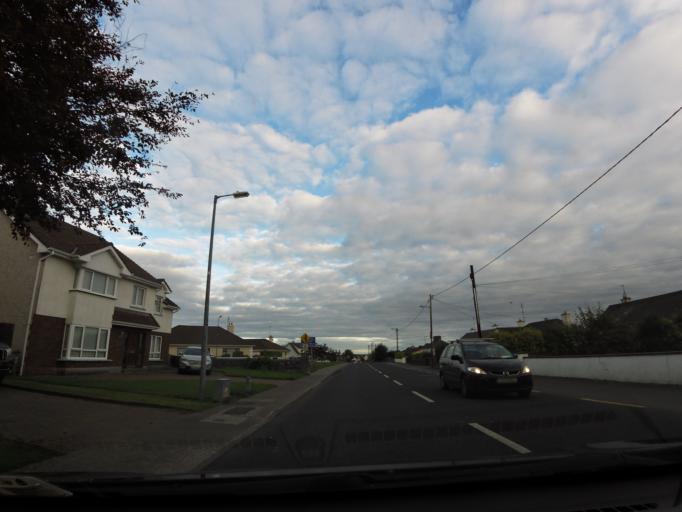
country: IE
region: Connaught
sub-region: County Galway
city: Athenry
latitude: 53.3024
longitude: -8.7542
